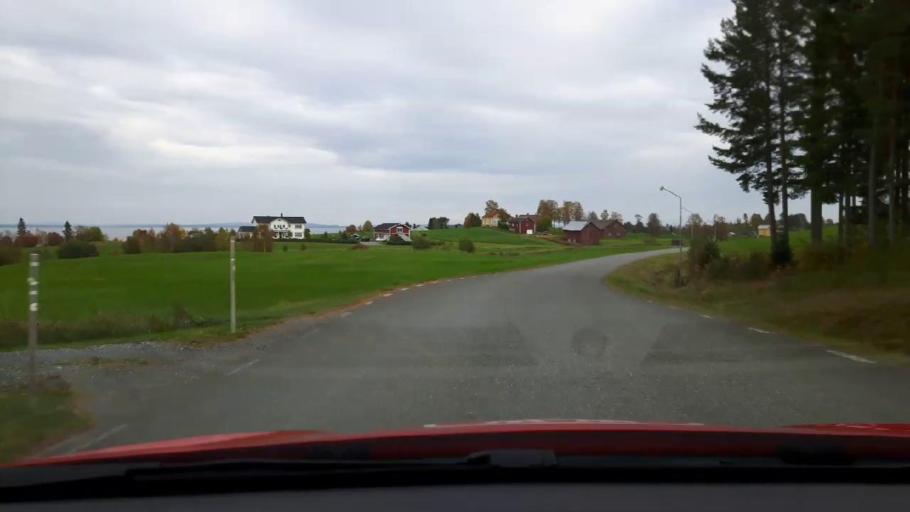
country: SE
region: Jaemtland
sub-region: Krokoms Kommun
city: Krokom
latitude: 63.2352
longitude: 14.1191
